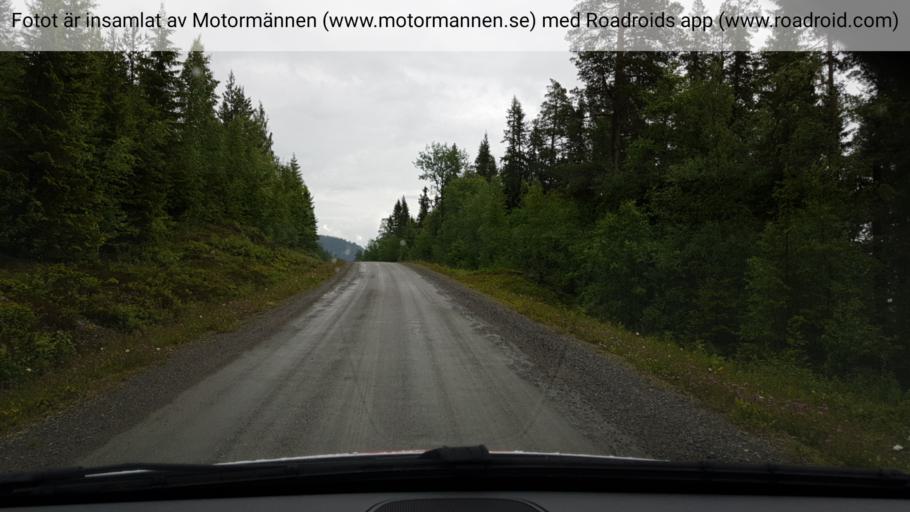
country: SE
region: Jaemtland
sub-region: Stroemsunds Kommun
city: Stroemsund
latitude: 64.2432
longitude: 15.0507
